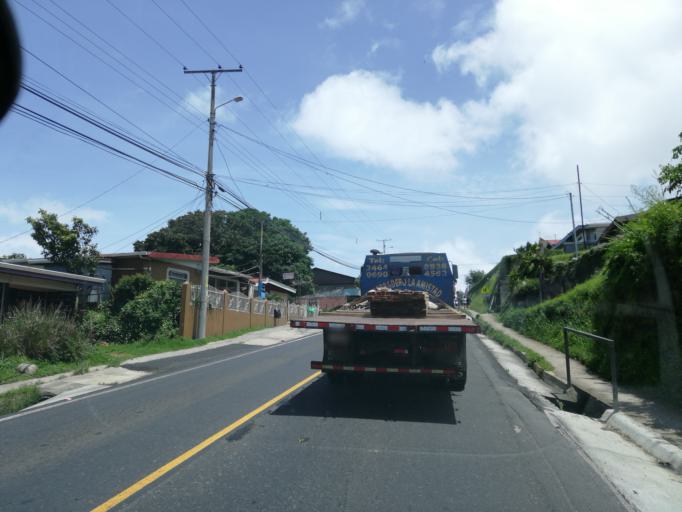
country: CR
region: Alajuela
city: Zarcero
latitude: 10.2171
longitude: -84.4014
